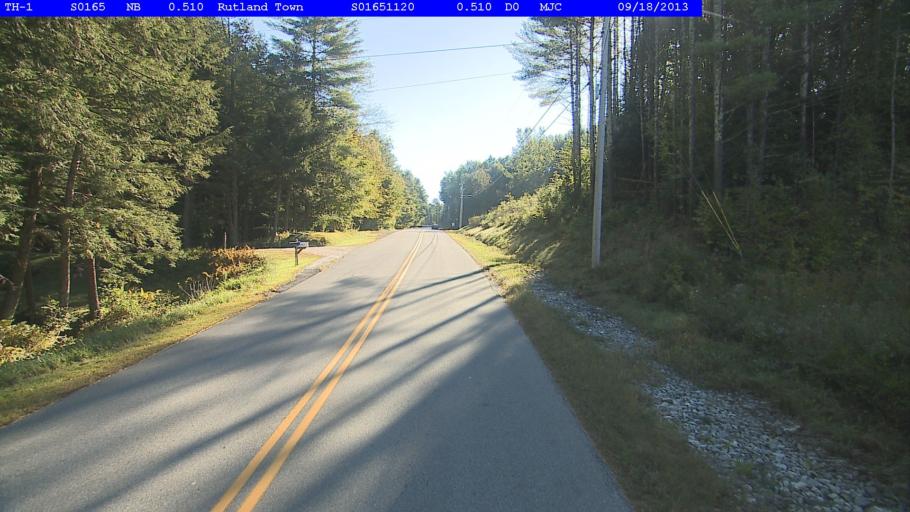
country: US
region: Vermont
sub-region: Rutland County
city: Rutland
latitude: 43.6520
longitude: -72.9621
